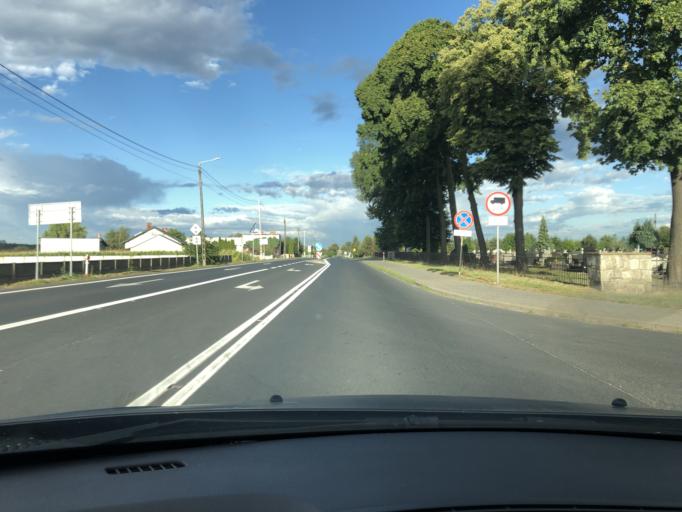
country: PL
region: Lodz Voivodeship
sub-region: Powiat wieruszowski
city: Sokolniki
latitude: 51.3048
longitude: 18.3165
